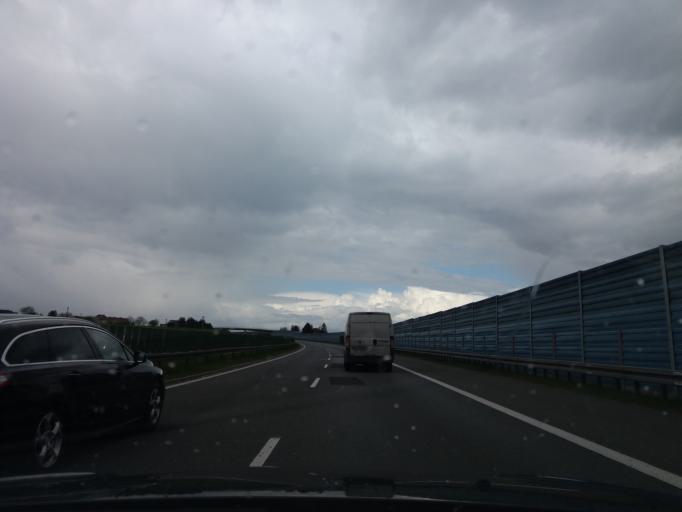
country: PL
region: Opole Voivodeship
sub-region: Powiat krapkowicki
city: Krapkowice
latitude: 50.5083
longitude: 17.9662
